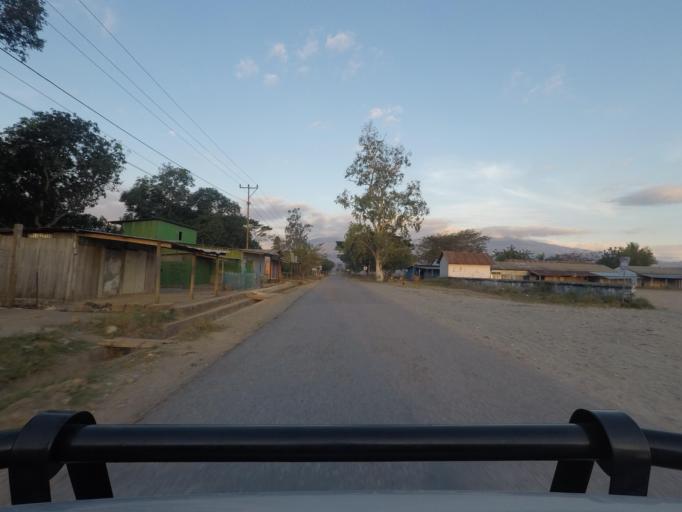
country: TL
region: Bobonaro
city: Maliana
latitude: -8.9761
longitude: 125.1422
